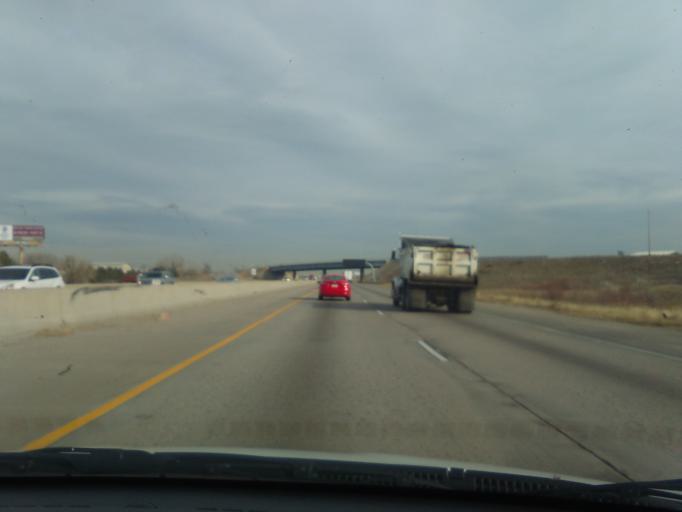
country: US
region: Colorado
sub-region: Adams County
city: Derby
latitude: 39.8442
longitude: -104.9265
